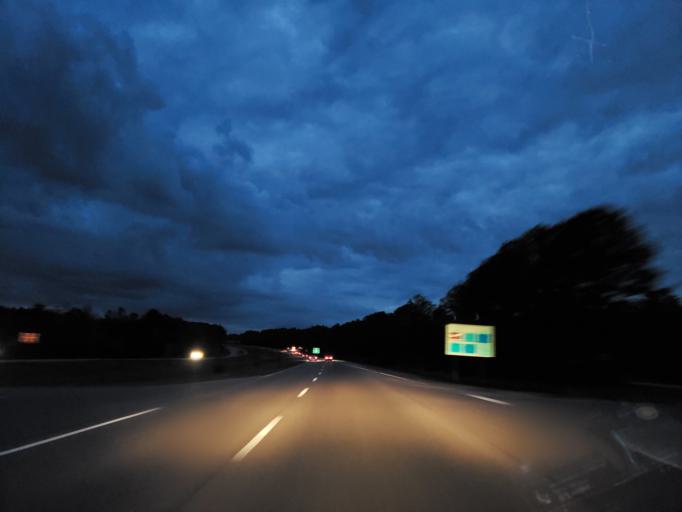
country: US
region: Mississippi
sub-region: Forrest County
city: Hattiesburg
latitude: 31.2463
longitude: -89.2653
